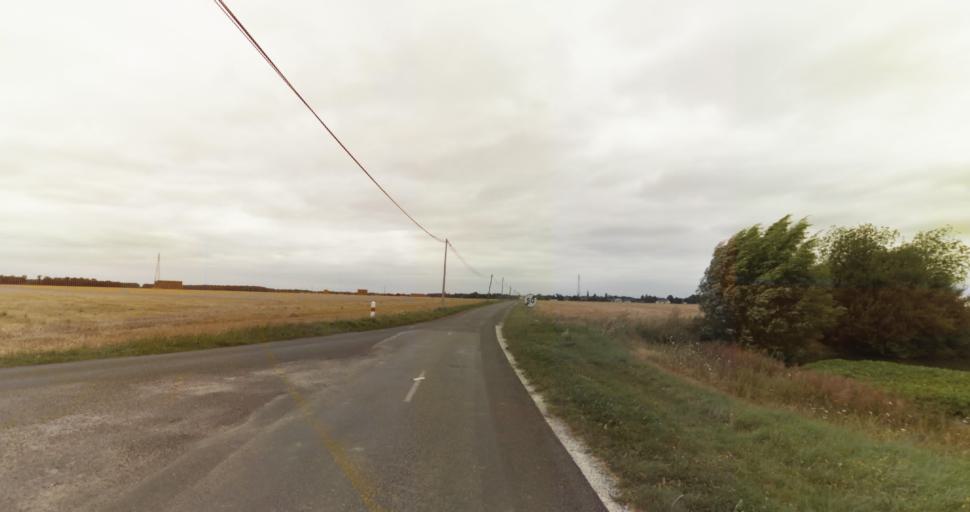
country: FR
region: Haute-Normandie
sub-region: Departement de l'Eure
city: Menilles
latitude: 48.9467
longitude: 1.2658
